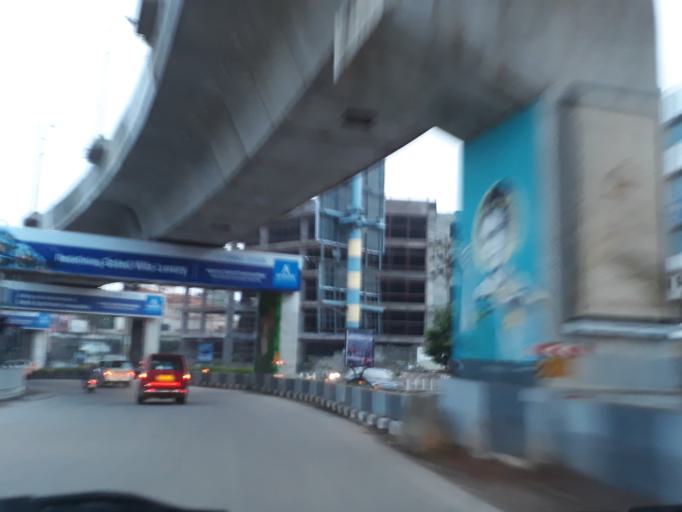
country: IN
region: Telangana
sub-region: Rangareddi
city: Kukatpalli
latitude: 17.4297
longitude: 78.4122
